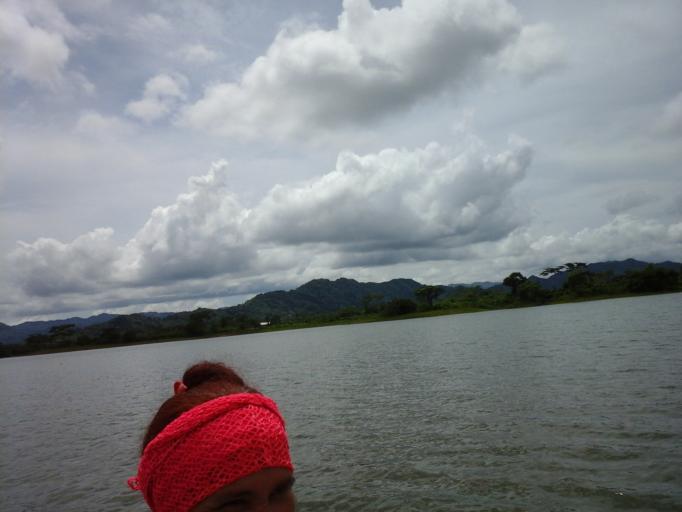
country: CO
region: Bolivar
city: San Cristobal
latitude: 9.8728
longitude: -75.2974
